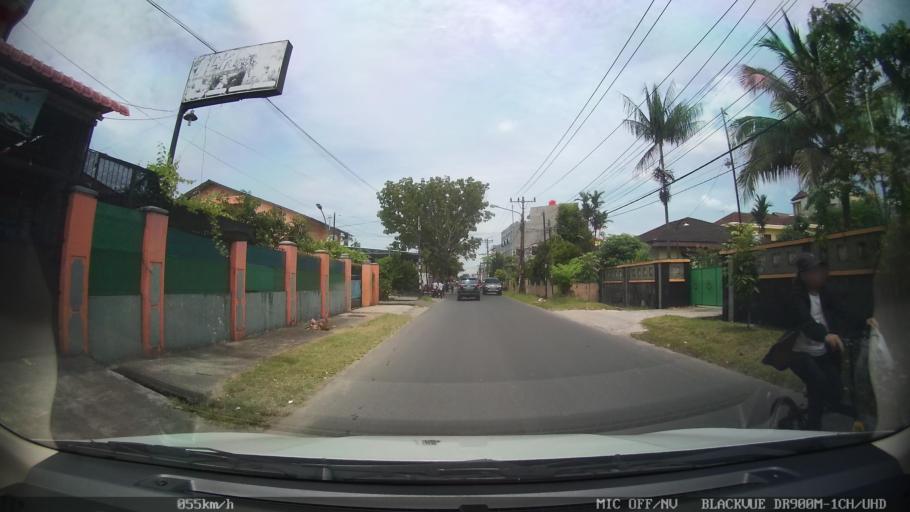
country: ID
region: North Sumatra
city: Sunggal
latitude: 3.5550
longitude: 98.6341
